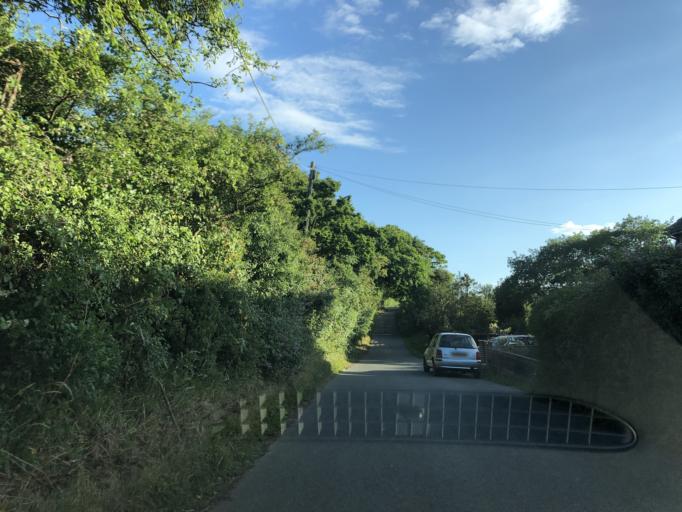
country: GB
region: England
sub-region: Isle of Wight
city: Yarmouth
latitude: 50.7028
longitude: -1.4685
